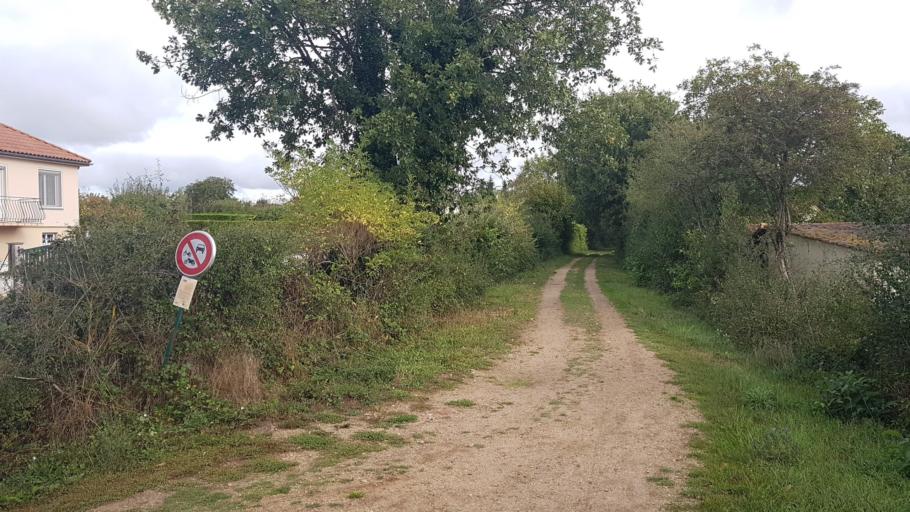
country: FR
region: Poitou-Charentes
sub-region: Departement de la Vienne
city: Saint-Savin
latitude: 46.5692
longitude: 0.8611
